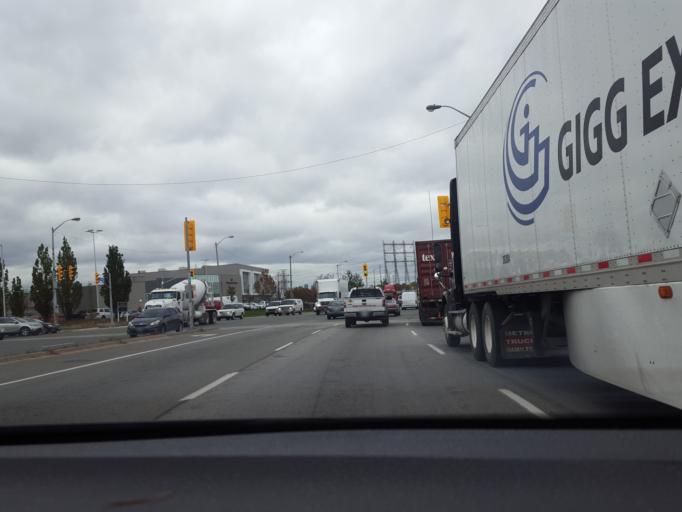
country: CA
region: Ontario
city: Etobicoke
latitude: 43.6144
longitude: -79.5555
